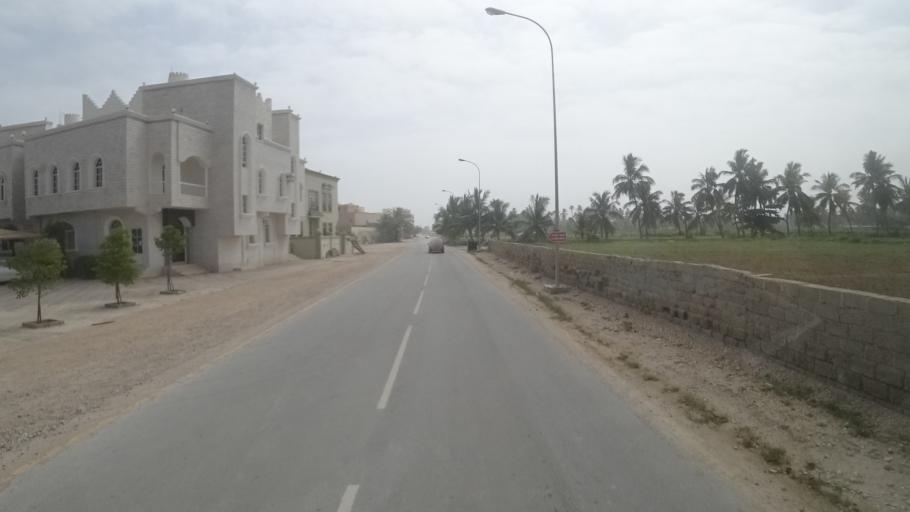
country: OM
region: Zufar
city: Salalah
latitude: 17.0126
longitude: 54.1636
